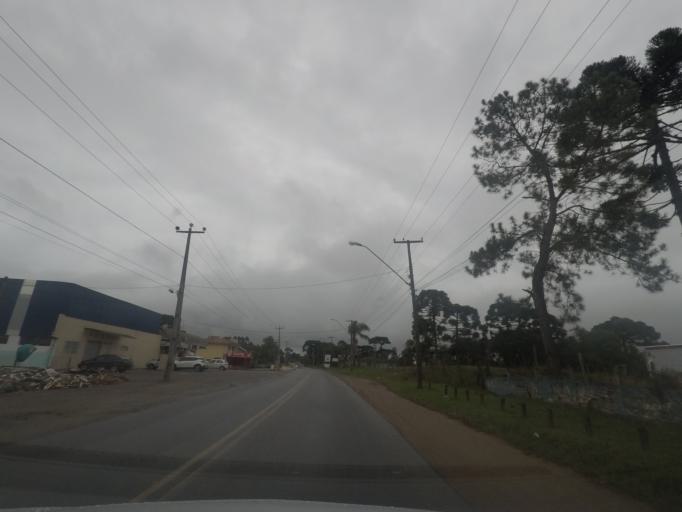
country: BR
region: Parana
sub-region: Quatro Barras
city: Quatro Barras
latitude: -25.3355
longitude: -49.0796
